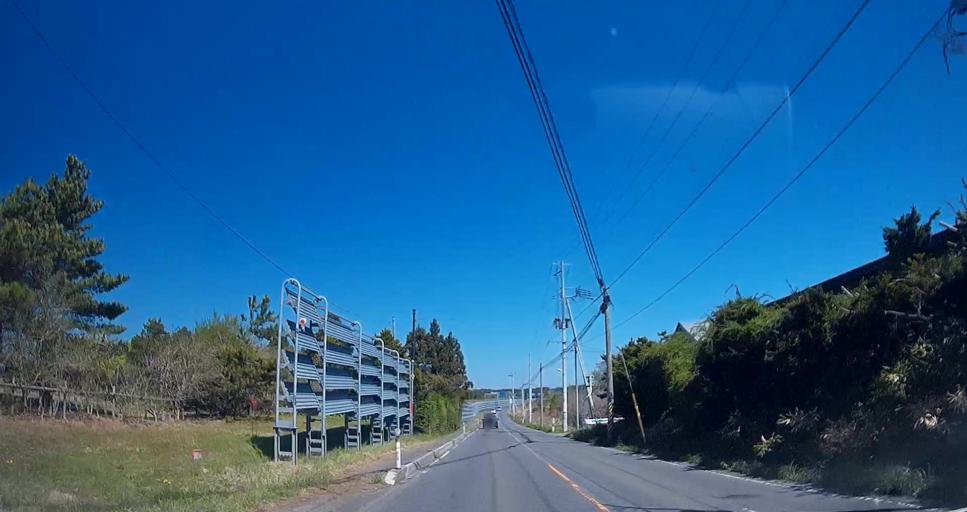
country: JP
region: Aomori
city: Misawa
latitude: 40.6919
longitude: 141.4248
